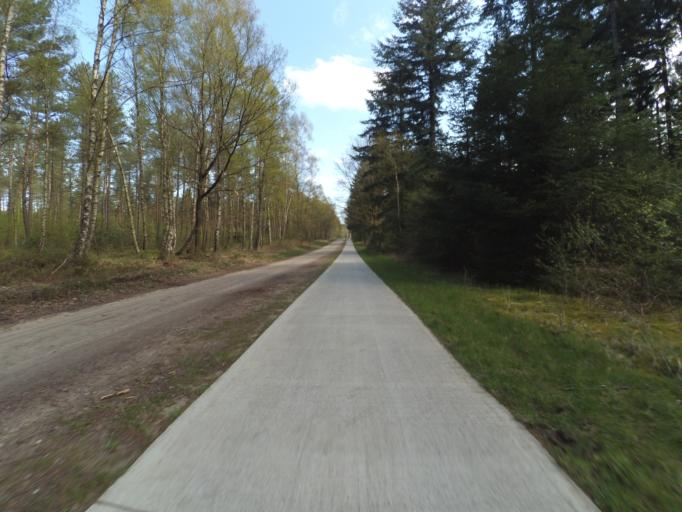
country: NL
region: Gelderland
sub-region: Gemeente Oldebroek
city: Oldebroek
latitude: 52.3687
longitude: 5.8987
